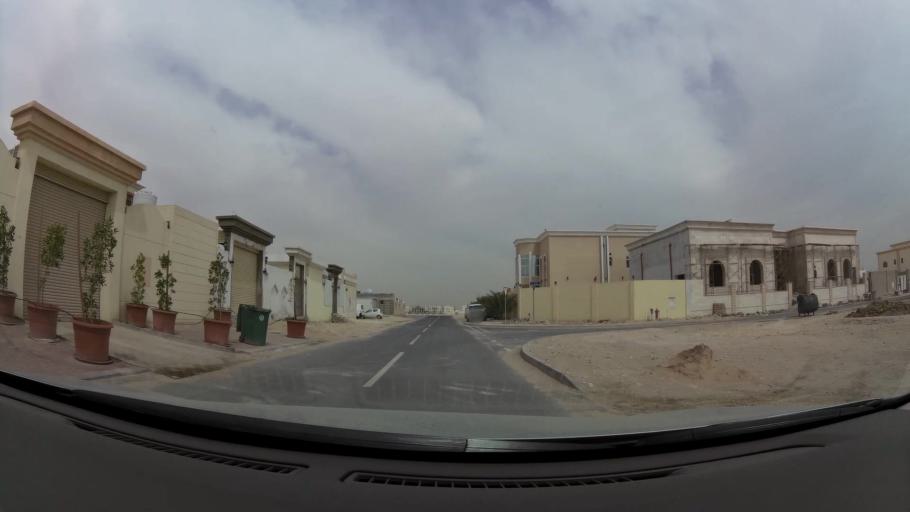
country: QA
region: Baladiyat ad Dawhah
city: Doha
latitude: 25.2101
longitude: 51.4660
